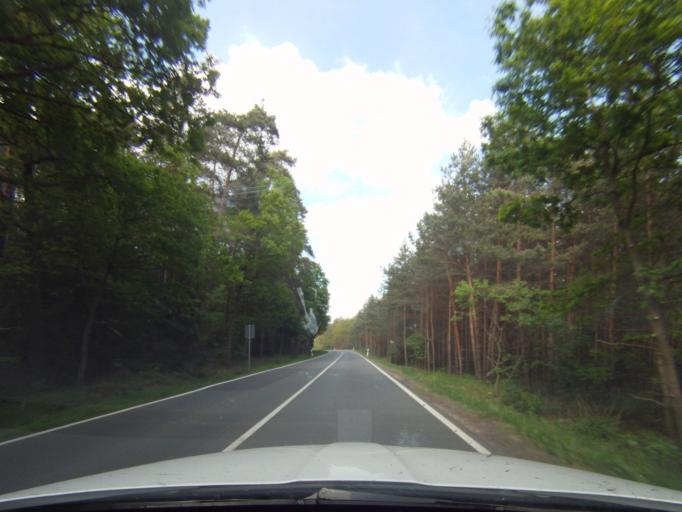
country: DE
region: Thuringia
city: Mittelpollnitz
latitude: 50.7724
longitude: 11.9327
